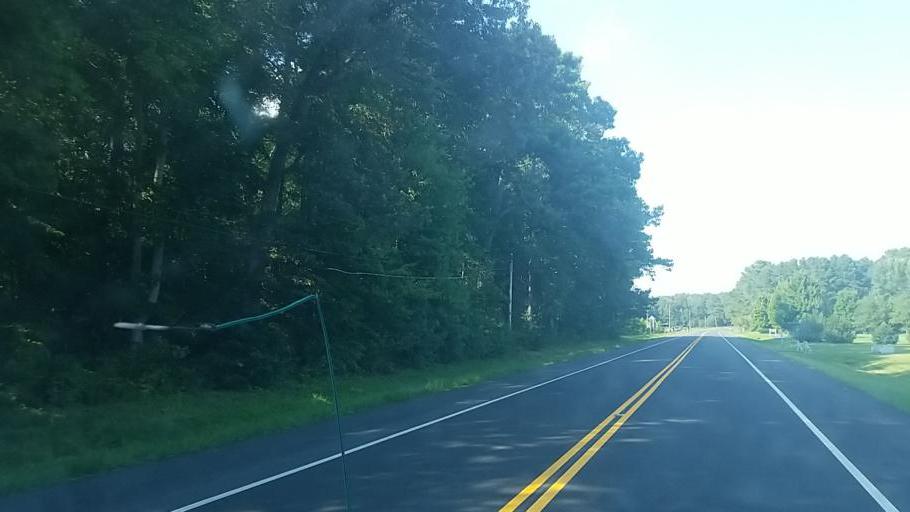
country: US
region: Maryland
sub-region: Worcester County
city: Berlin
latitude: 38.3659
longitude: -75.2010
